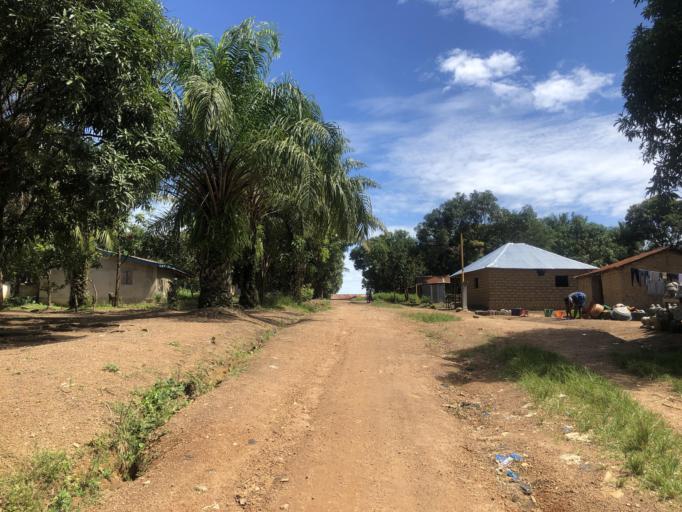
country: SL
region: Eastern Province
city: Koidu
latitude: 8.6394
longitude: -10.9480
